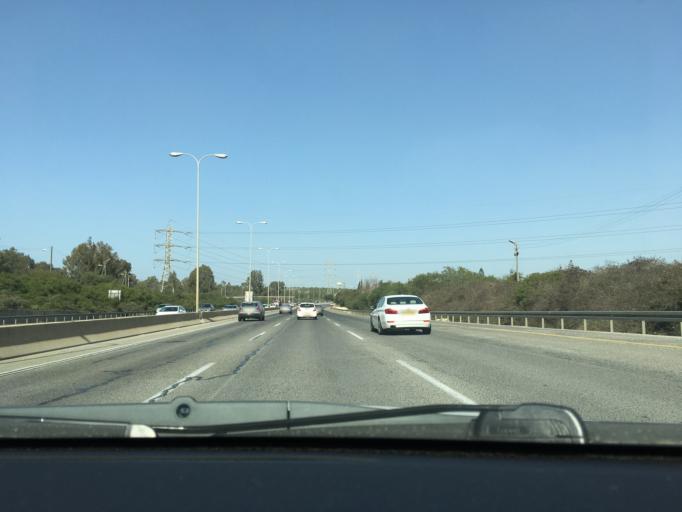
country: IL
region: Tel Aviv
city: Ramat HaSharon
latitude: 32.1319
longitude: 34.8711
